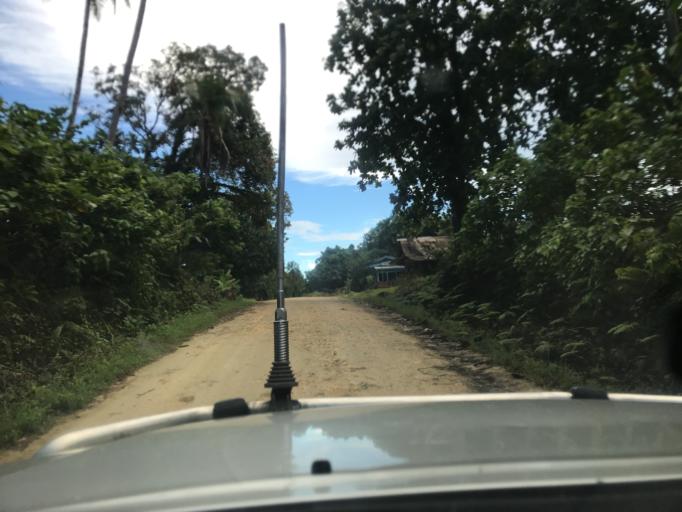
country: SB
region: Malaita
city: Auki
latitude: -8.6332
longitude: 160.6653
